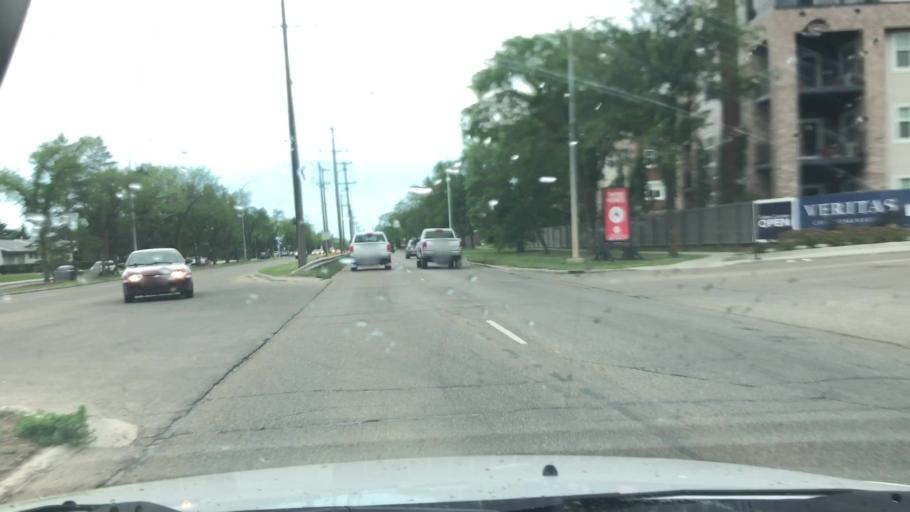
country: CA
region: Alberta
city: Edmonton
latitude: 53.5995
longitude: -113.4974
